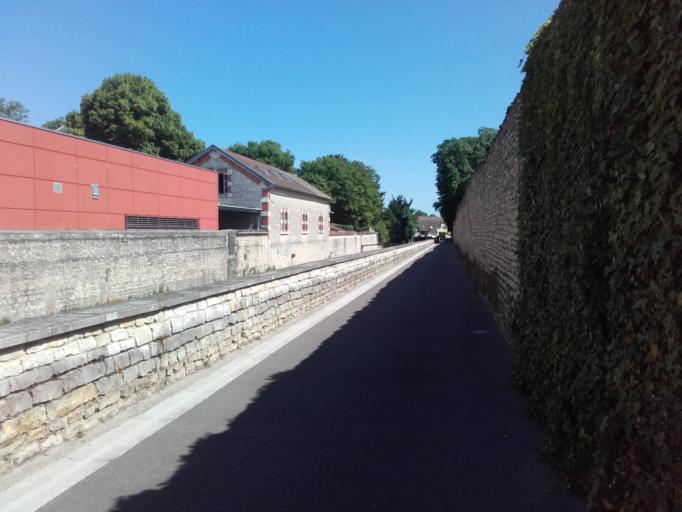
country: FR
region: Bourgogne
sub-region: Departement de la Cote-d'Or
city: Nuits-Saint-Georges
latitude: 47.1330
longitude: 4.9498
